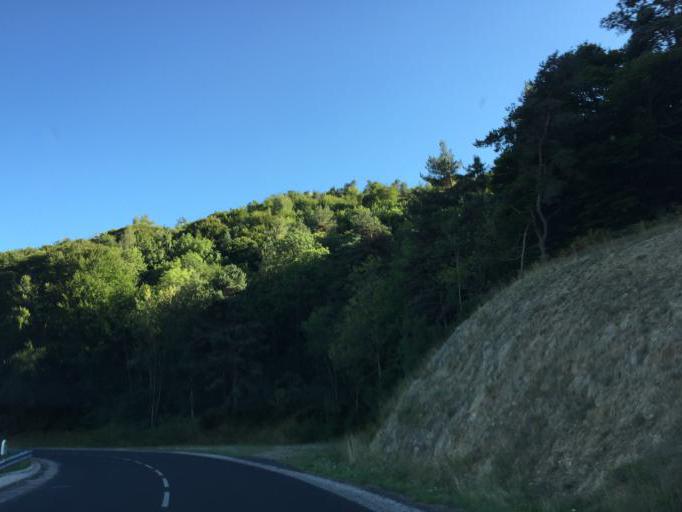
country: FR
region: Auvergne
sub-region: Departement de la Haute-Loire
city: Saugues
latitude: 44.9760
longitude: 3.6269
